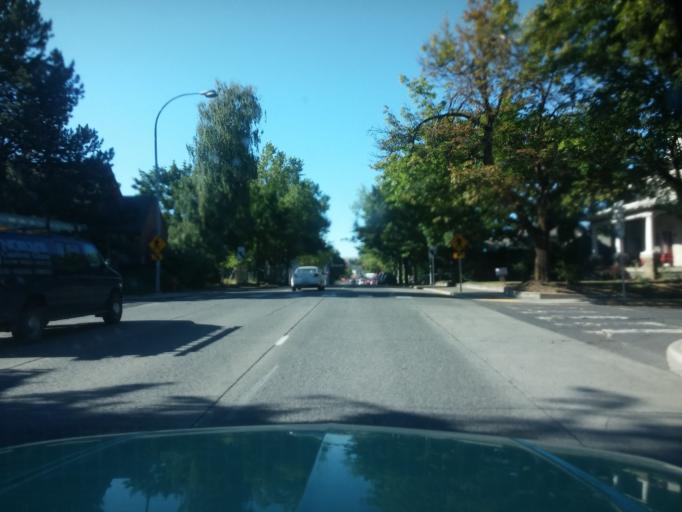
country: US
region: Idaho
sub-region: Latah County
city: Moscow
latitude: 46.7339
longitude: -117.0028
